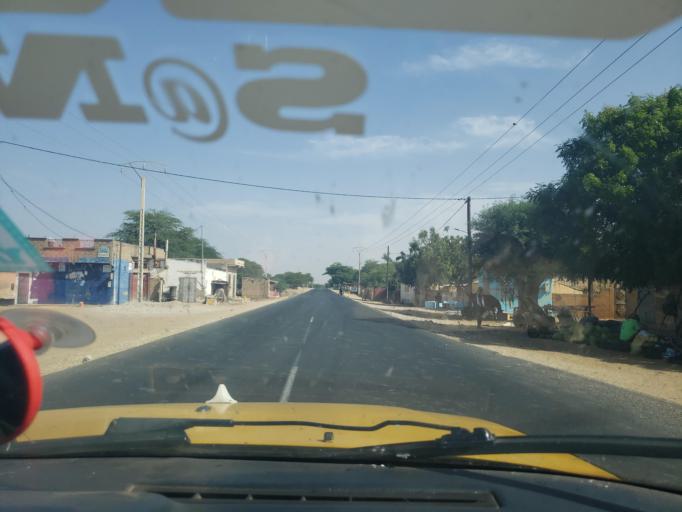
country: SN
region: Saint-Louis
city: Saint-Louis
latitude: 15.9284
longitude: -16.3242
